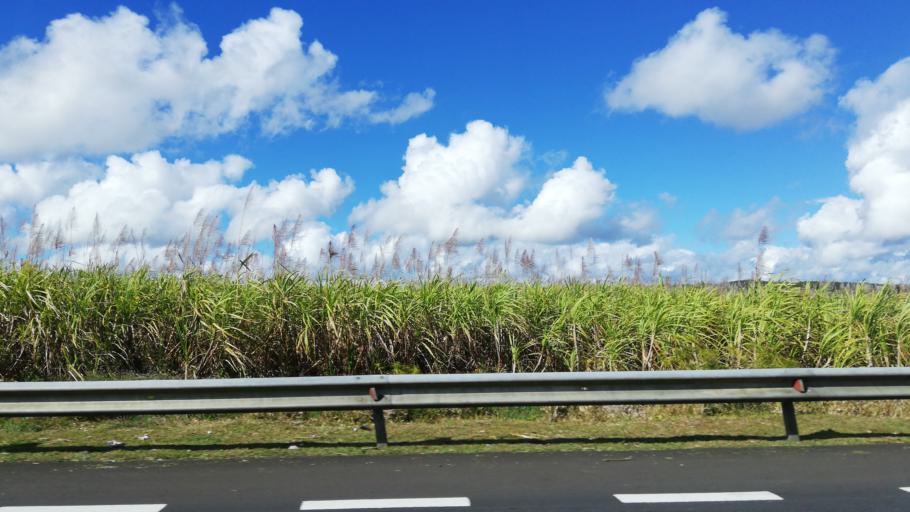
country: MU
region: Moka
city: Quartier Militaire
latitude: -20.2552
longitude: 57.5766
